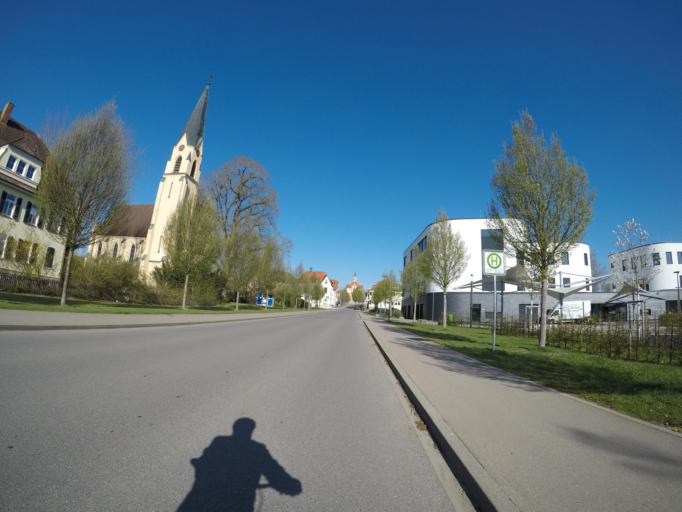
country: DE
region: Baden-Wuerttemberg
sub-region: Tuebingen Region
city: Altshausen
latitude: 47.9337
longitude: 9.5421
